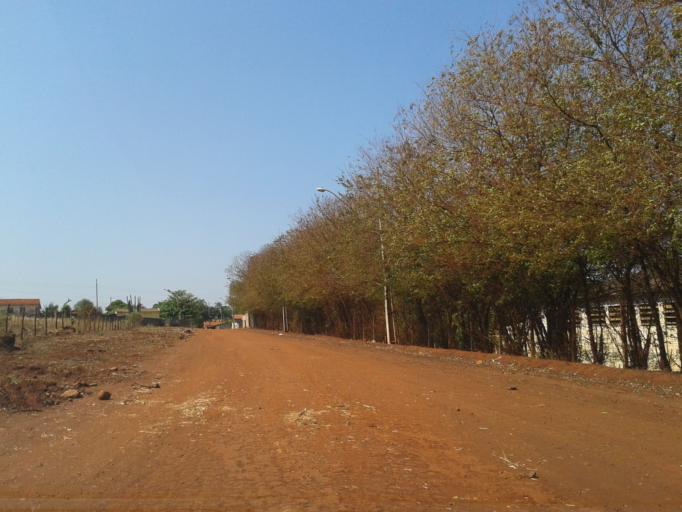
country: BR
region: Minas Gerais
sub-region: Ituiutaba
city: Ituiutaba
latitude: -18.9542
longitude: -49.4532
